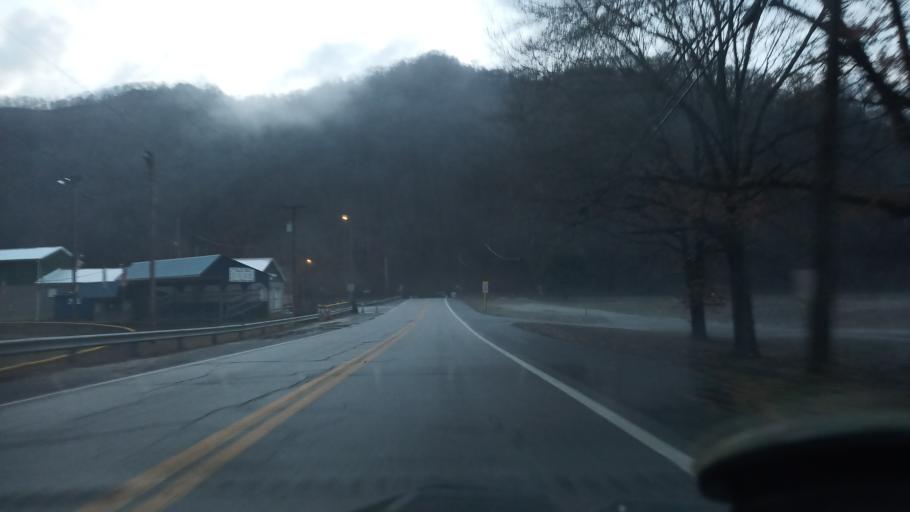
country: US
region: West Virginia
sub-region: Logan County
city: Mallory
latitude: 37.7306
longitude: -81.8746
